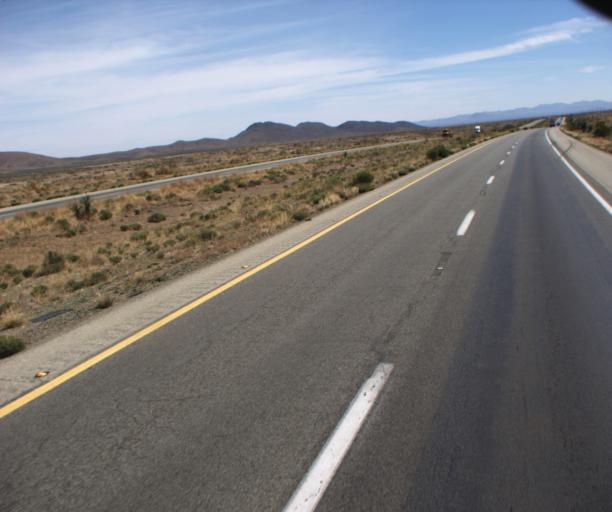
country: US
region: Arizona
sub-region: Cochise County
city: Willcox
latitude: 32.3623
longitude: -109.6487
